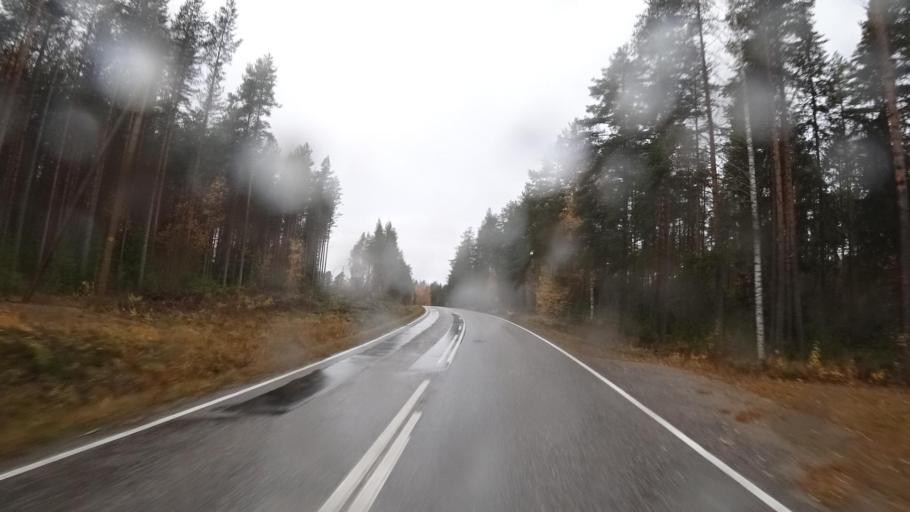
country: FI
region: North Karelia
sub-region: Joensuu
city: Outokumpu
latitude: 62.6206
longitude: 28.9230
